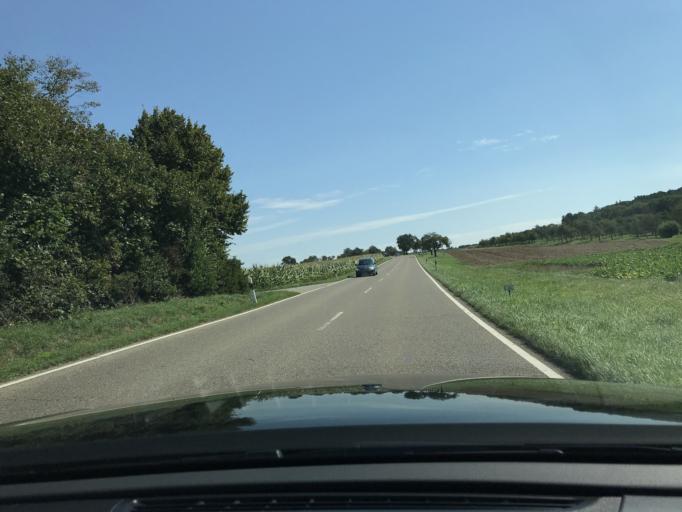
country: DE
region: Baden-Wuerttemberg
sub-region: Regierungsbezirk Stuttgart
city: Erdmannhausen
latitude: 48.9285
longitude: 9.3009
